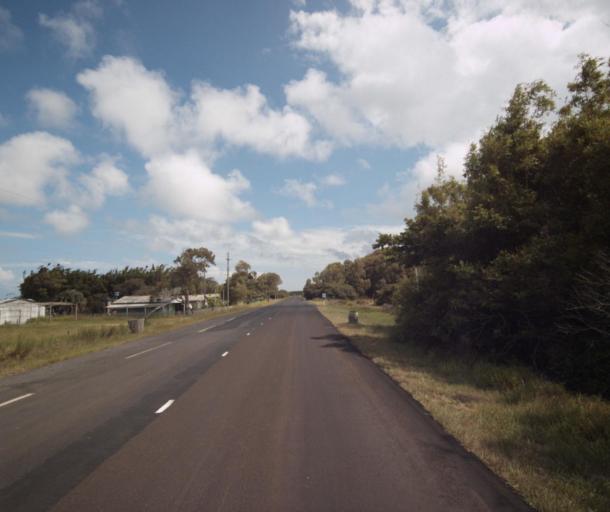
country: BR
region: Rio Grande do Sul
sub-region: Tapes
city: Tapes
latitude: -31.4047
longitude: -51.1658
